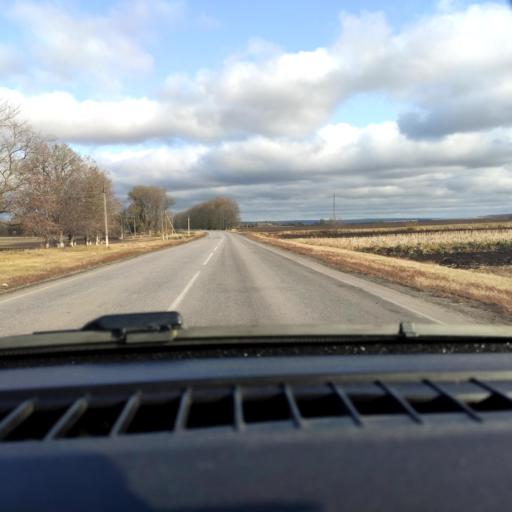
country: RU
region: Belgorod
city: Ilovka
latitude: 50.7383
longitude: 38.7057
